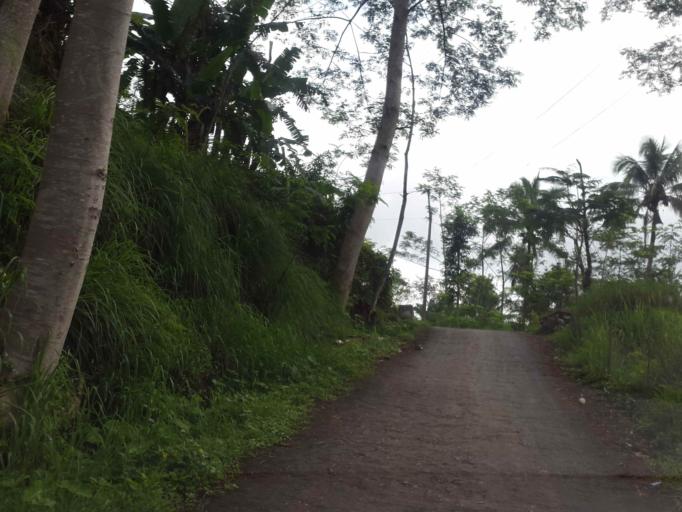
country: ID
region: Central Java
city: Cigintung
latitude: -7.2350
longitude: 108.6977
